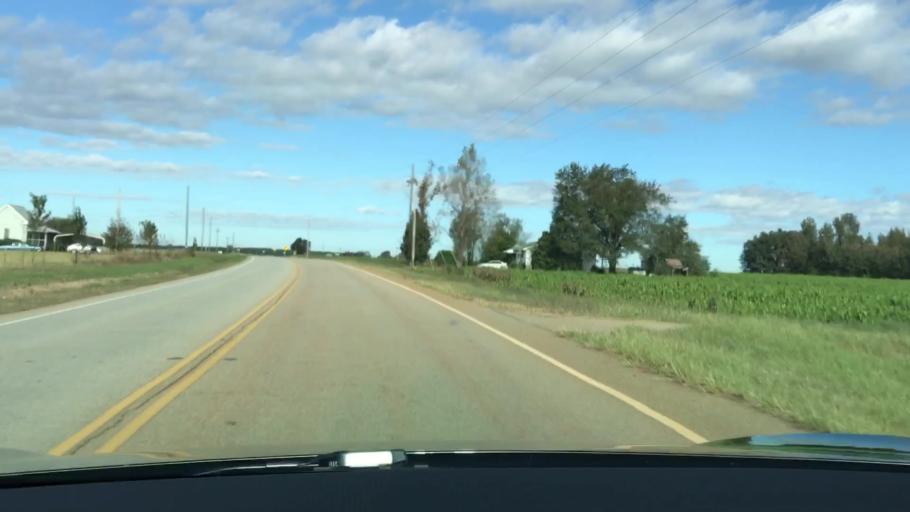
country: US
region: Georgia
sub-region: Jefferson County
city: Louisville
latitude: 33.0979
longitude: -82.4199
